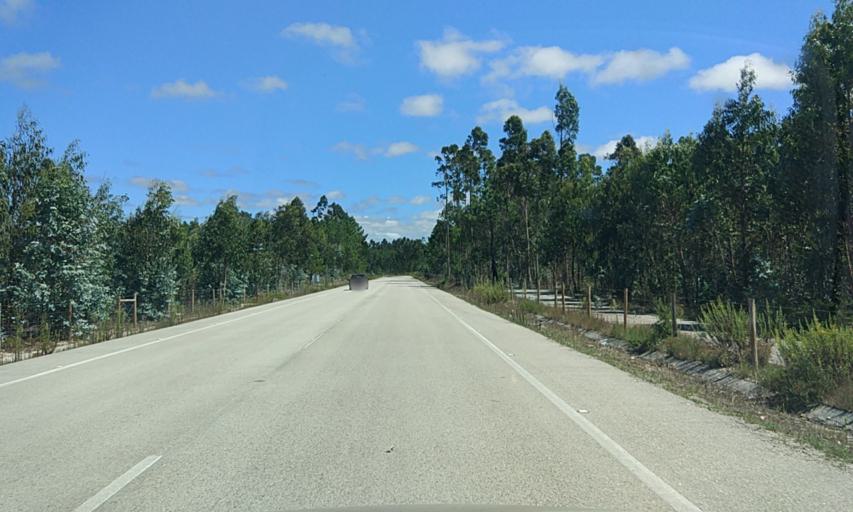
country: PT
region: Coimbra
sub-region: Mira
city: Mira
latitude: 40.3381
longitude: -8.7419
